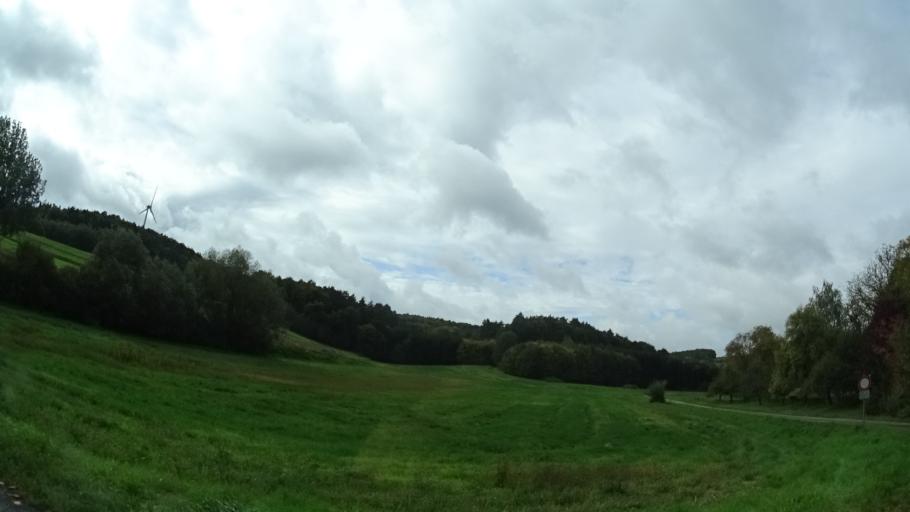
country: DE
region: Bavaria
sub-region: Upper Franconia
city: Priesendorf
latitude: 49.9222
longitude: 10.7406
